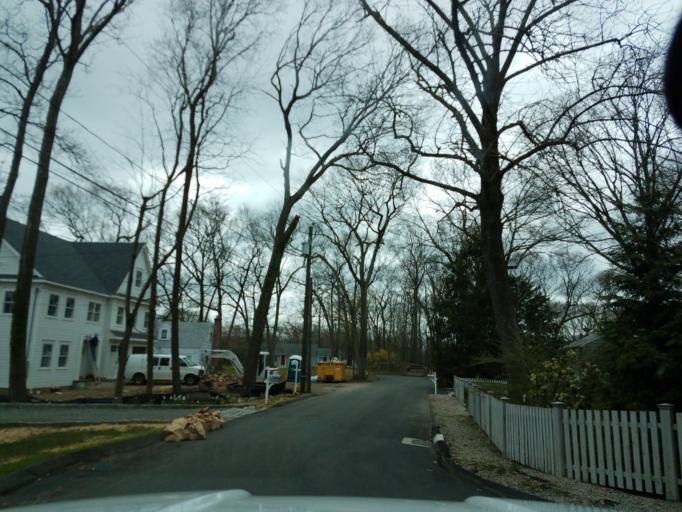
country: US
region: Connecticut
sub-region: Fairfield County
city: Darien
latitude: 41.0813
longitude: -73.4404
